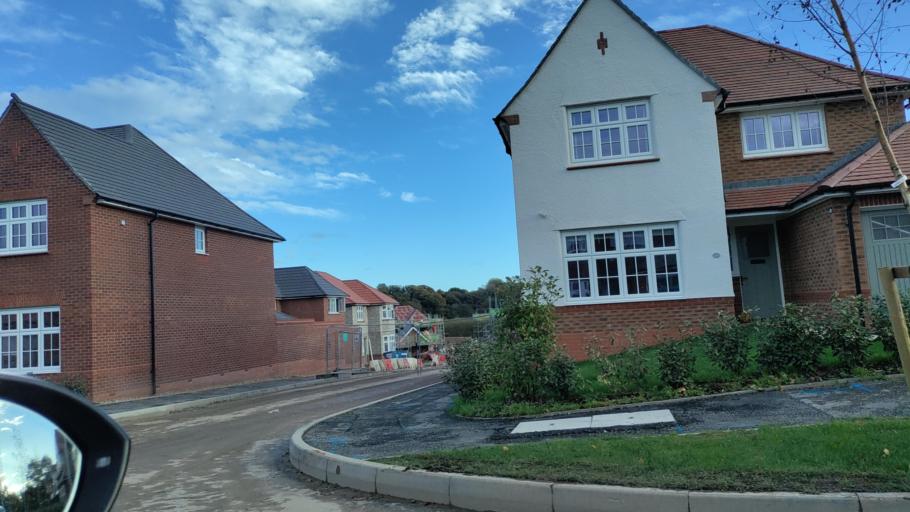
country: GB
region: England
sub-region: Cheshire West and Chester
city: Hartford
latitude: 53.2408
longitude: -2.5321
